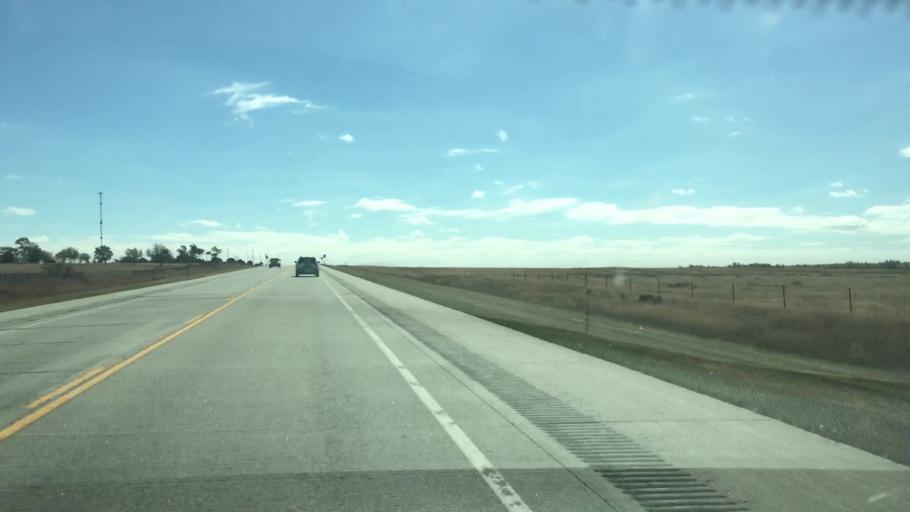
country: US
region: Colorado
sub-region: Lincoln County
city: Hugo
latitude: 39.1474
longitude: -103.4973
